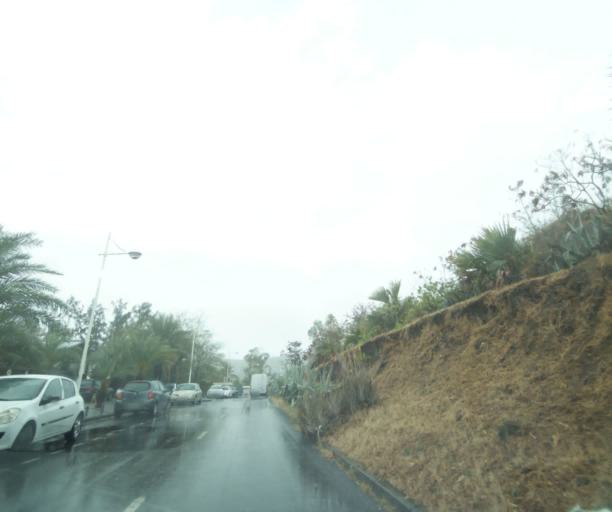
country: RE
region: Reunion
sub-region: Reunion
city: Saint-Paul
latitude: -21.0320
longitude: 55.2236
